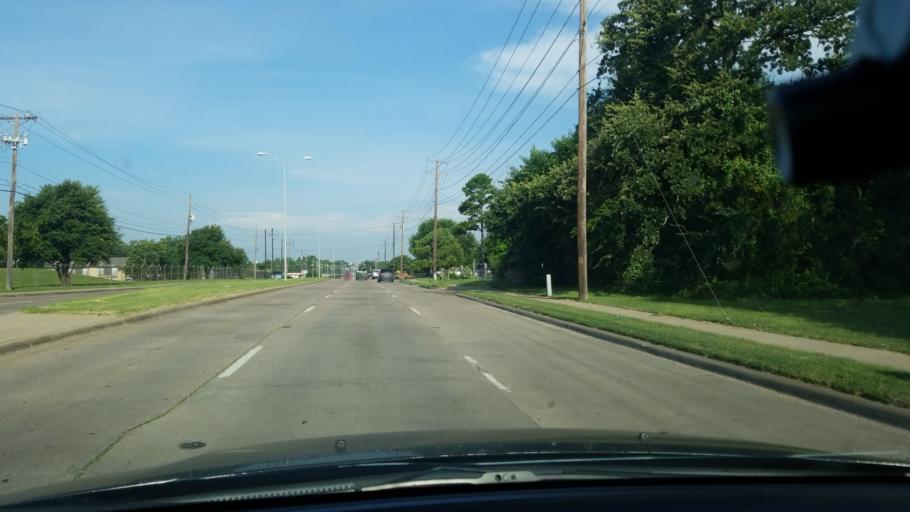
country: US
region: Texas
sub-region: Dallas County
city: Balch Springs
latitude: 32.7342
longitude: -96.6522
